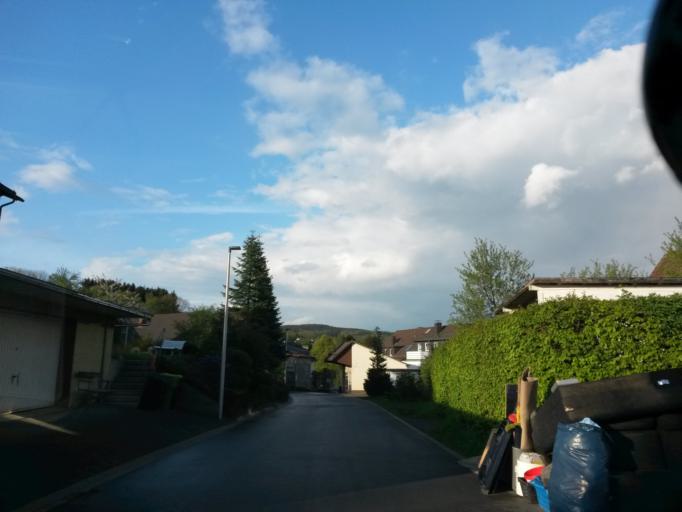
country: DE
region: North Rhine-Westphalia
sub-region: Regierungsbezirk Arnsberg
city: Herscheid
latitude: 51.1191
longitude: 7.7494
